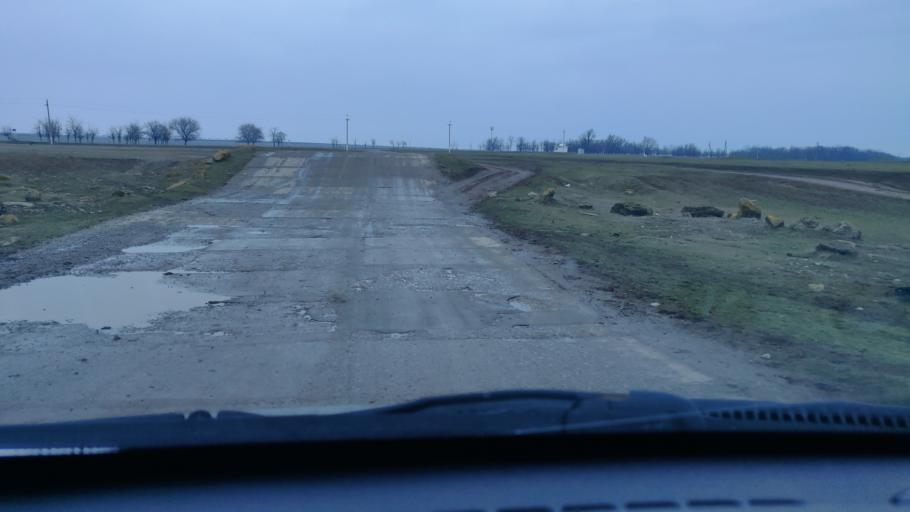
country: RU
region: Stavropol'skiy
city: Letnyaya Stavka
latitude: 45.4125
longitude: 43.7048
